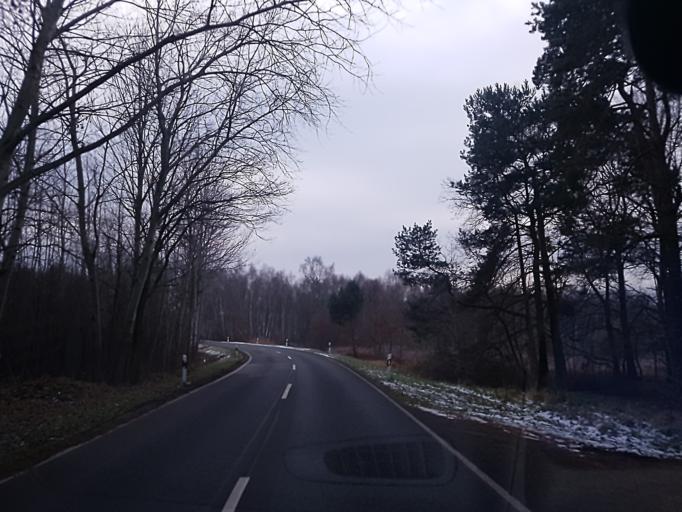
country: DE
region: Brandenburg
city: Crinitz
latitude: 51.7383
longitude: 13.8440
